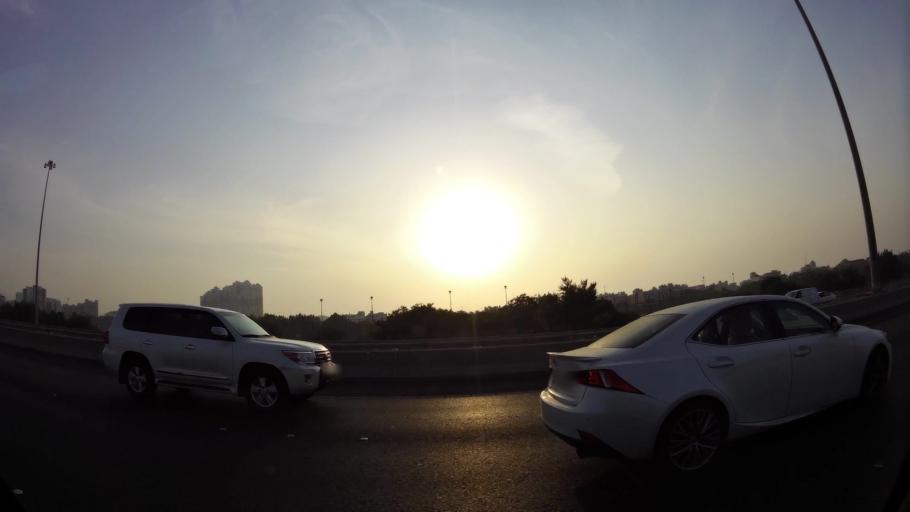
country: KW
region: Muhafazat Hawalli
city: Salwa
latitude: 29.2721
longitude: 48.0836
